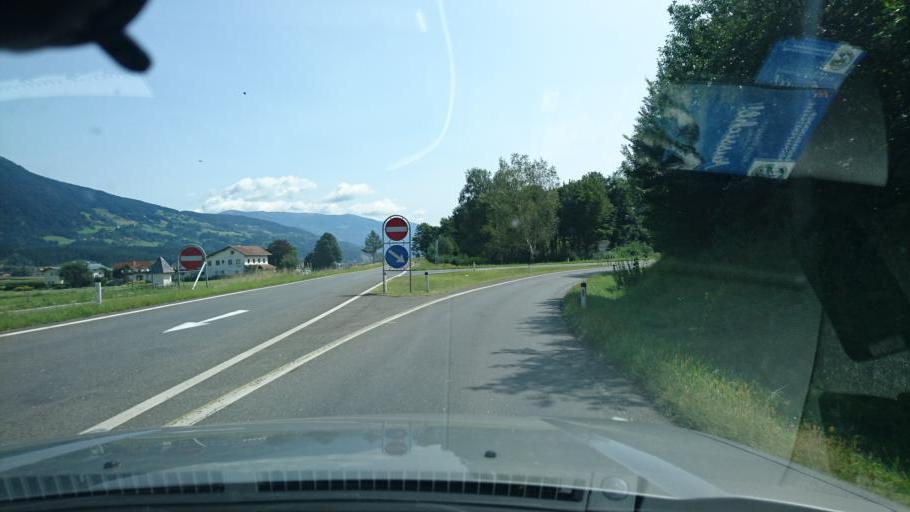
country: AT
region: Carinthia
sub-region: Politischer Bezirk Spittal an der Drau
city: Sachsenburg
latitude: 46.8323
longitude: 13.3820
